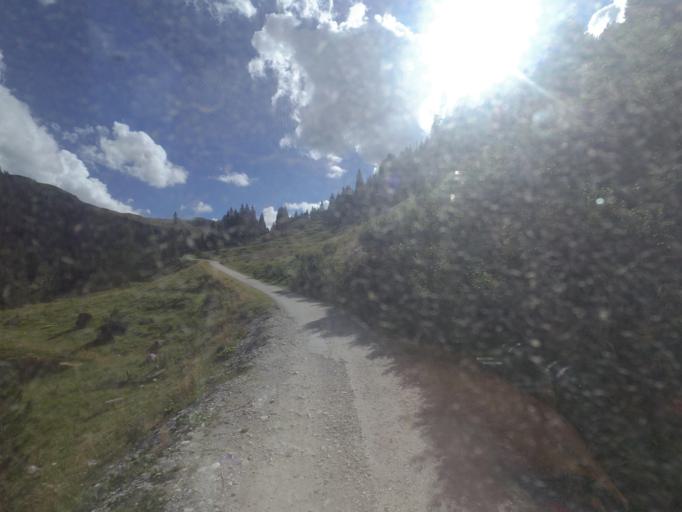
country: AT
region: Salzburg
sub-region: Politischer Bezirk Sankt Johann im Pongau
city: Kleinarl
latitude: 47.1790
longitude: 13.3539
